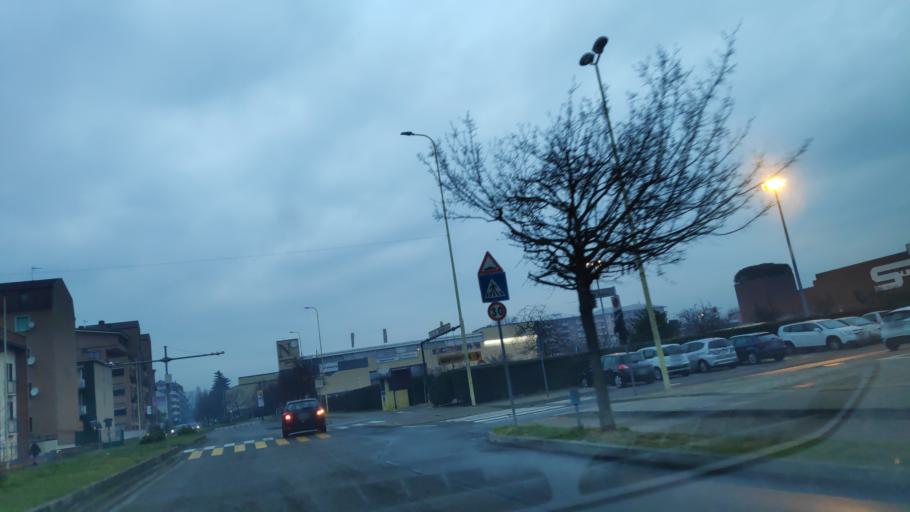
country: IT
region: Lombardy
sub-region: Citta metropolitana di Milano
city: Romano Banco
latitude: 45.4326
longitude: 9.1199
